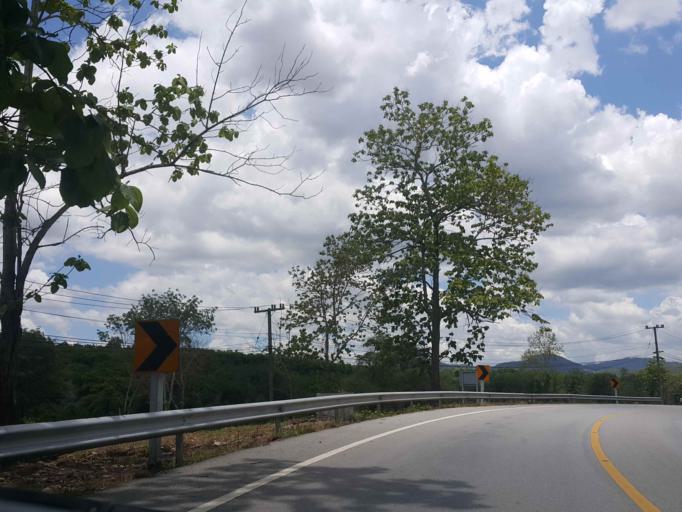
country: TH
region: Nan
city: Wiang Sa
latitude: 18.5248
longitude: 100.6142
